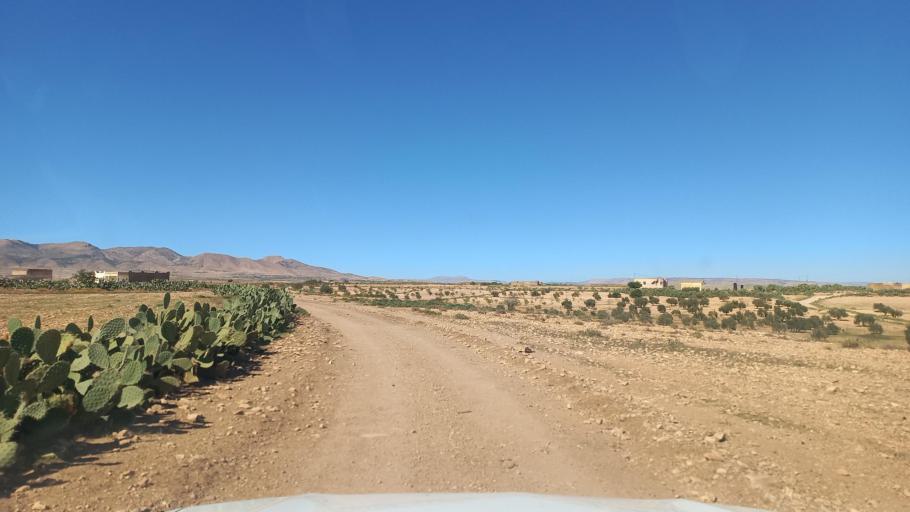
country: TN
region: Al Qasrayn
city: Sbiba
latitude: 35.3800
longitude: 9.0891
